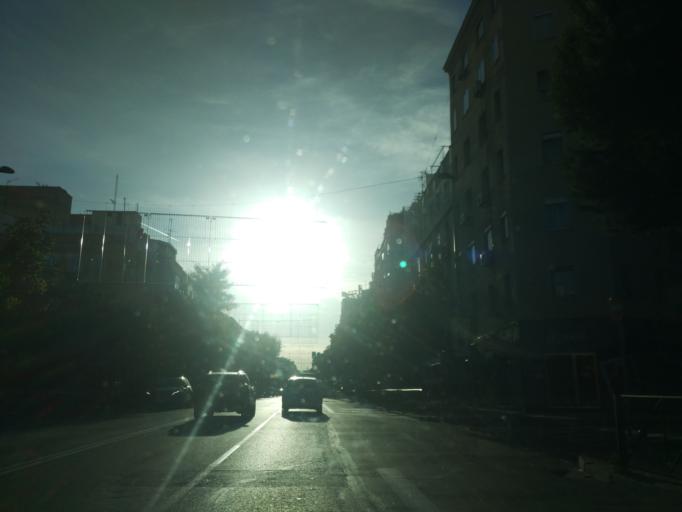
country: ES
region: Madrid
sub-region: Provincia de Madrid
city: Carabanchel
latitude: 40.3967
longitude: -3.7178
